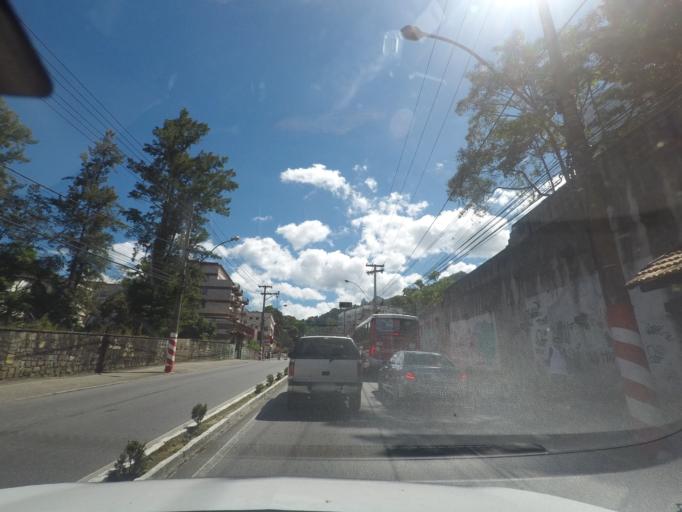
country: BR
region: Rio de Janeiro
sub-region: Teresopolis
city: Teresopolis
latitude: -22.4253
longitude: -42.9792
